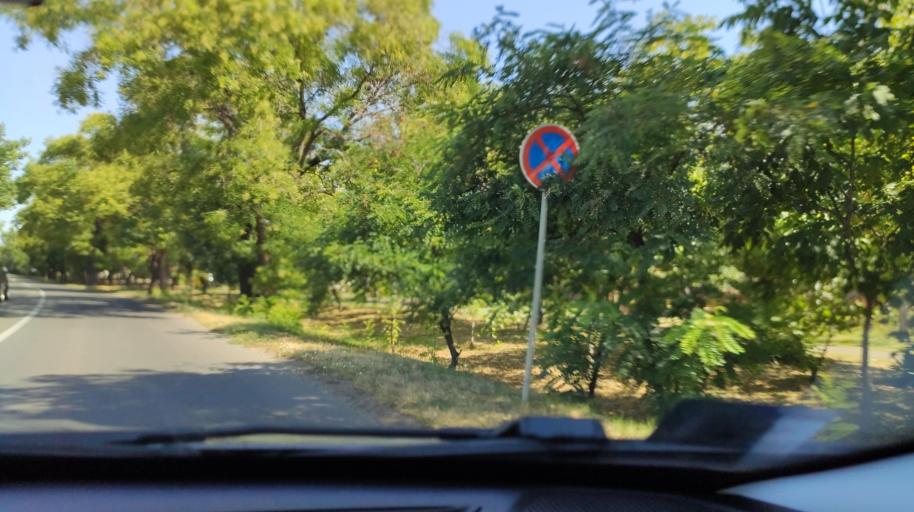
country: RS
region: Autonomna Pokrajina Vojvodina
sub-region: Severnobacki Okrug
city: Backa Topola
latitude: 45.8234
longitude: 19.6318
